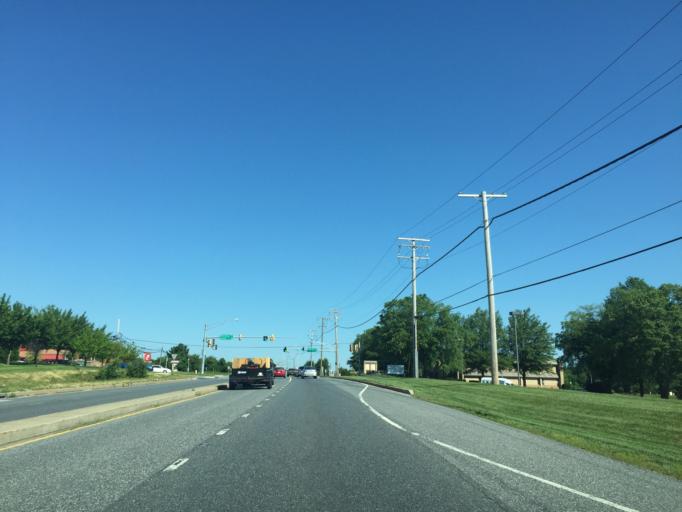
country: US
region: Maryland
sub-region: Harford County
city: Bel Air North
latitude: 39.5702
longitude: -76.3798
